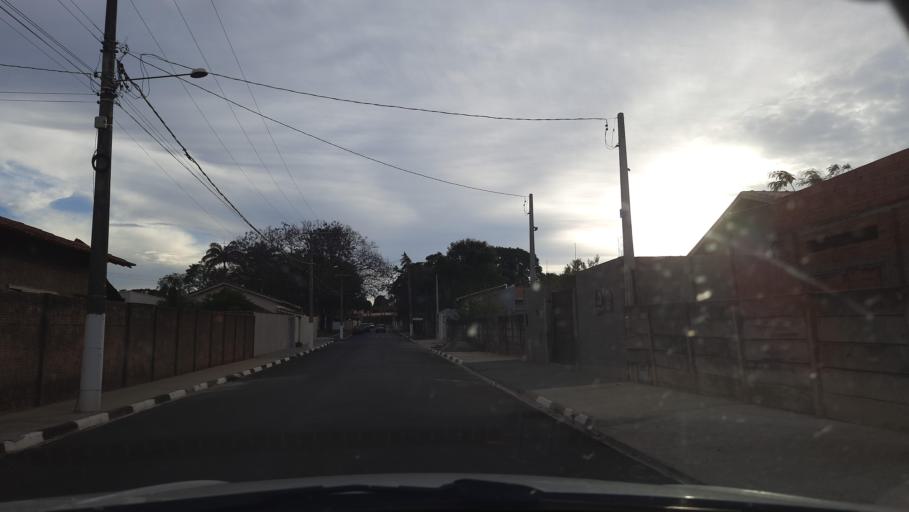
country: BR
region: Sao Paulo
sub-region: Casa Branca
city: Casa Branca
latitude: -21.7799
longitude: -47.0650
